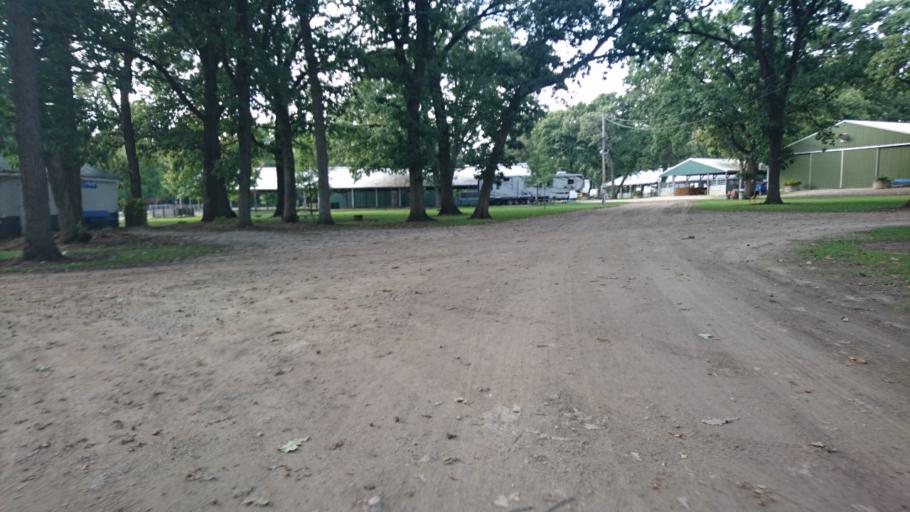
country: US
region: Illinois
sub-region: Livingston County
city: Pontiac
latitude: 40.8914
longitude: -88.6641
